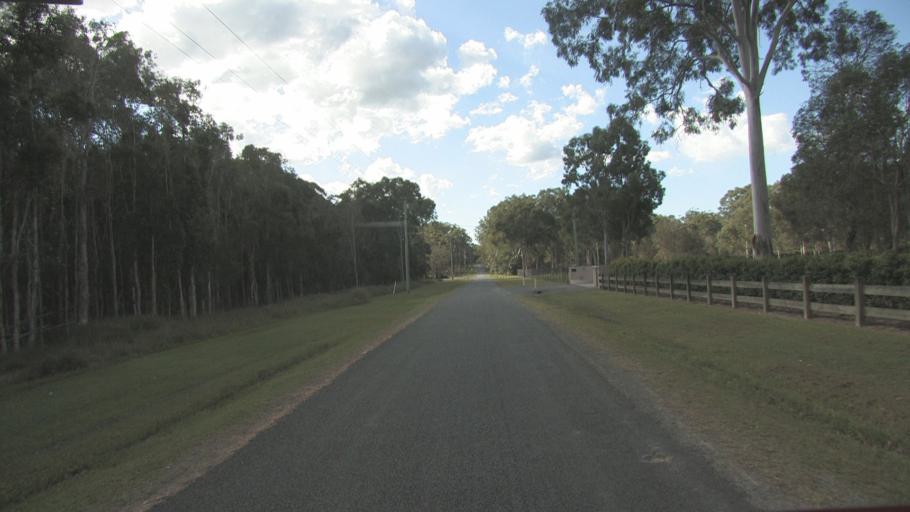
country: AU
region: Queensland
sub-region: Gold Coast
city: Yatala
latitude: -27.6629
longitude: 153.2411
